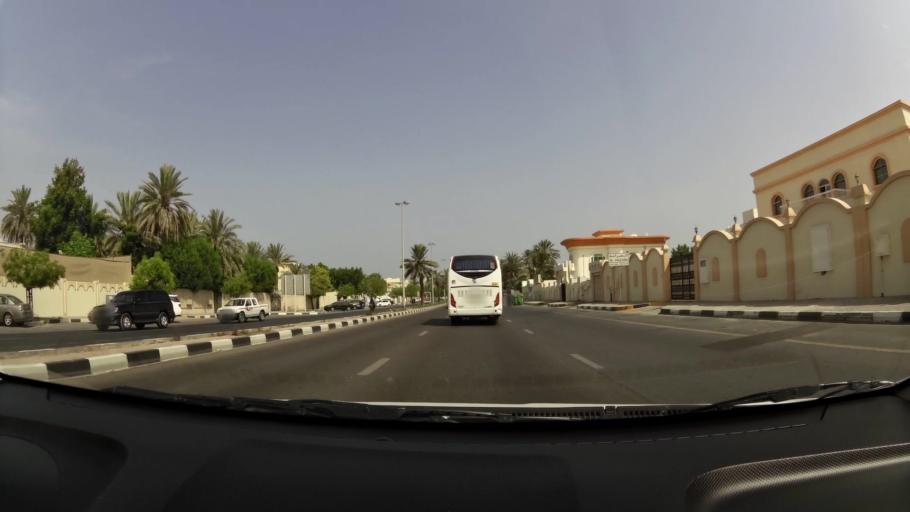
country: AE
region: Ash Shariqah
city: Sharjah
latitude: 25.3655
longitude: 55.4187
